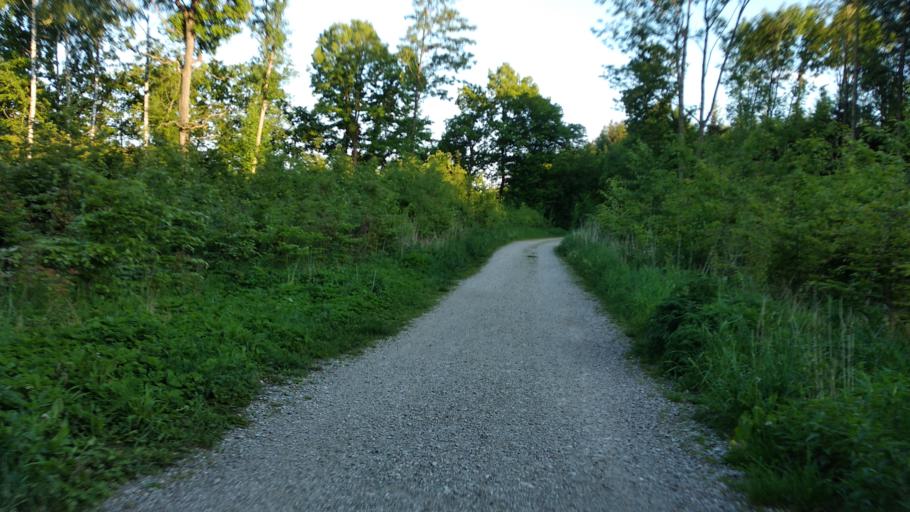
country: DE
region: Bavaria
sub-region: Upper Bavaria
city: Zorneding
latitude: 48.0928
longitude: 11.8022
